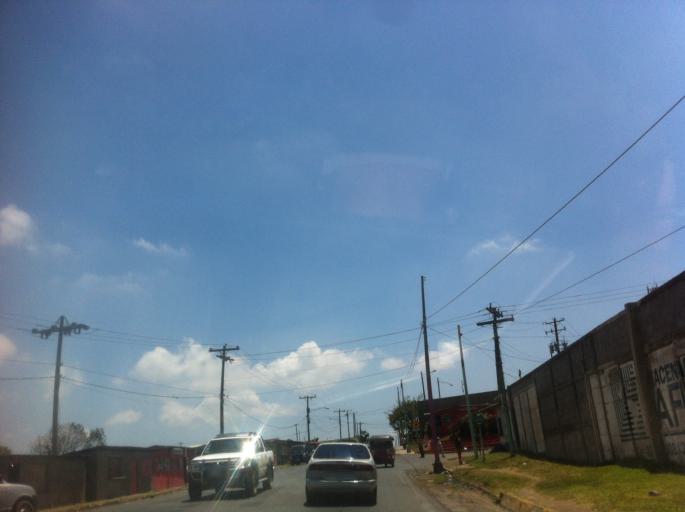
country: NI
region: Managua
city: El Crucero
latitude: 11.9934
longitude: -86.3095
